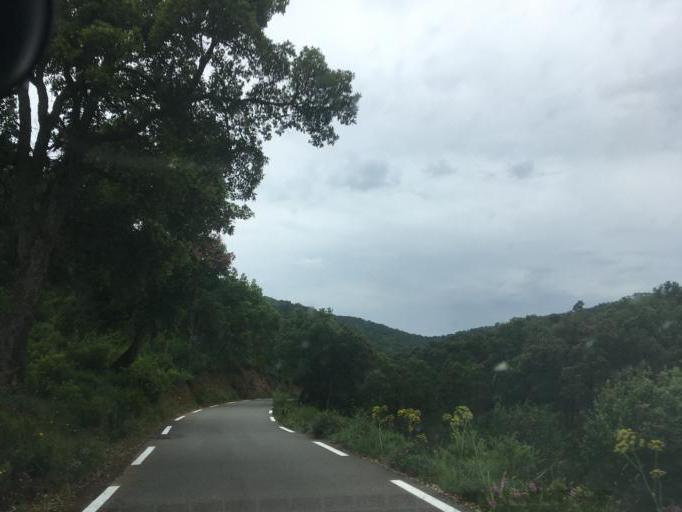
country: FR
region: Provence-Alpes-Cote d'Azur
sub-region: Departement du Var
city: Pierrefeu-du-Var
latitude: 43.2092
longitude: 6.2124
